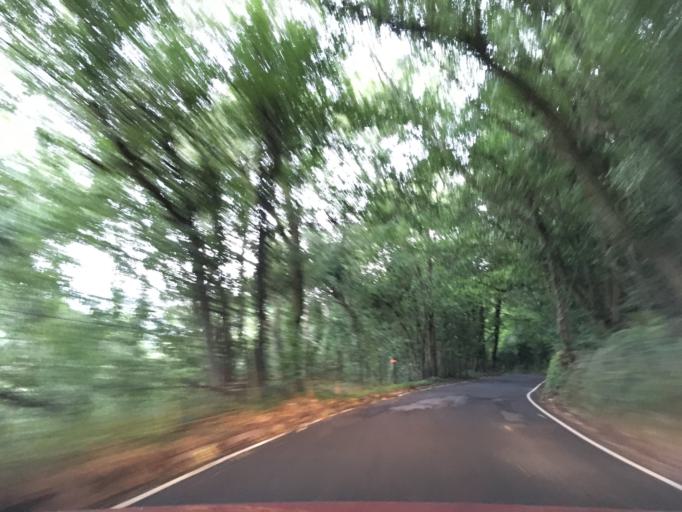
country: GB
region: Wales
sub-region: Newport
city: Llanvaches
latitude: 51.6521
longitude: -2.8547
